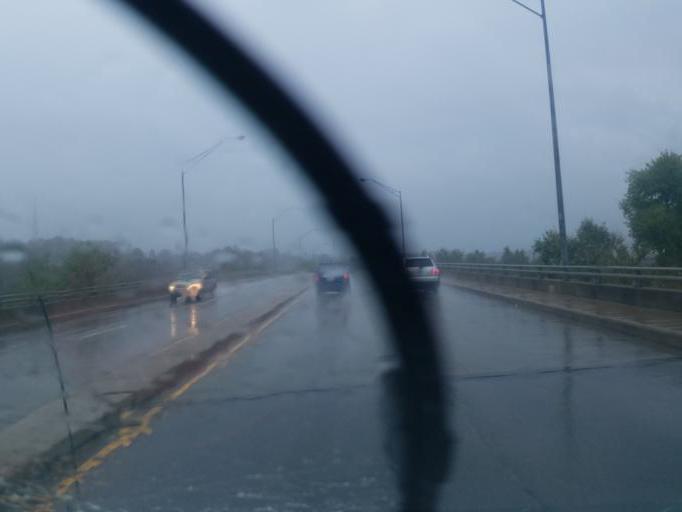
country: US
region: Ohio
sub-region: Muskingum County
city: Zanesville
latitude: 39.9511
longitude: -82.0026
